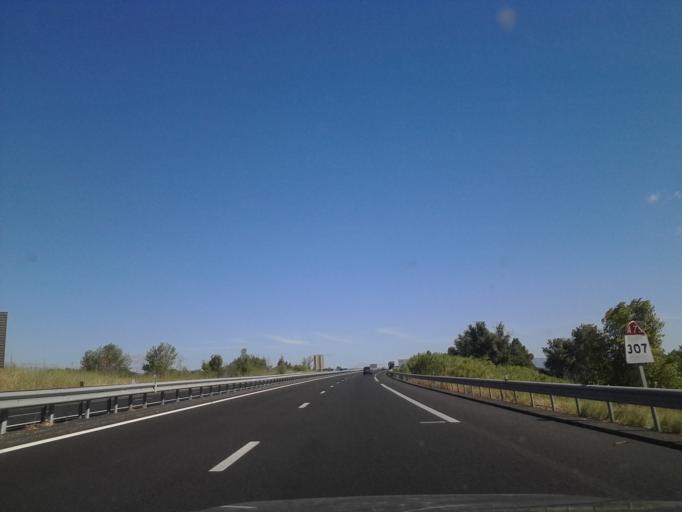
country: FR
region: Languedoc-Roussillon
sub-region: Departement de l'Herault
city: Lezignan-la-Cebe
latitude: 43.5073
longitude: 3.4436
